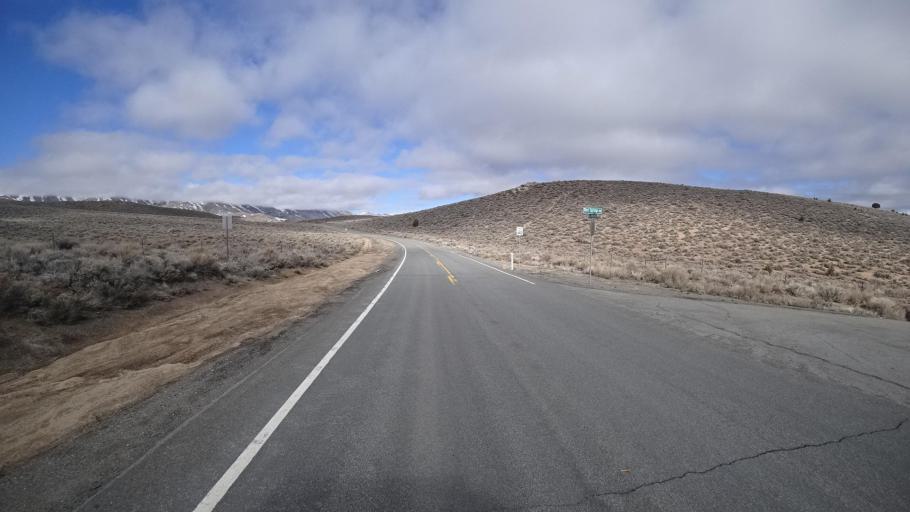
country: US
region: Nevada
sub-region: Washoe County
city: Cold Springs
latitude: 39.8001
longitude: -119.9034
